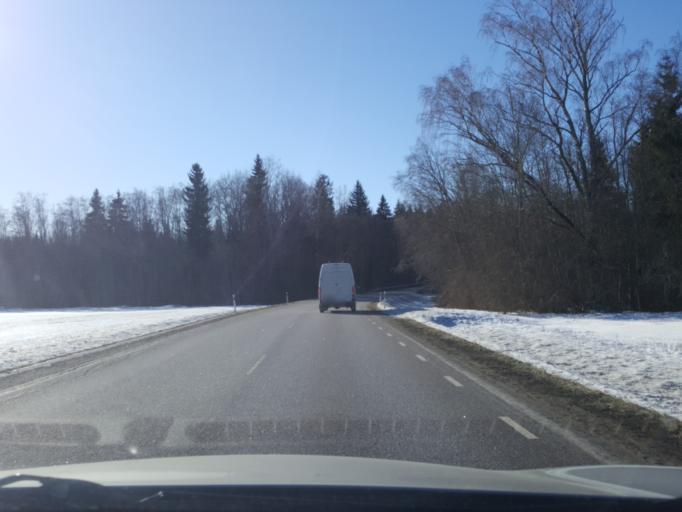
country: EE
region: Viljandimaa
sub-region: Viiratsi vald
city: Viiratsi
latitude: 58.4175
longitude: 25.6758
